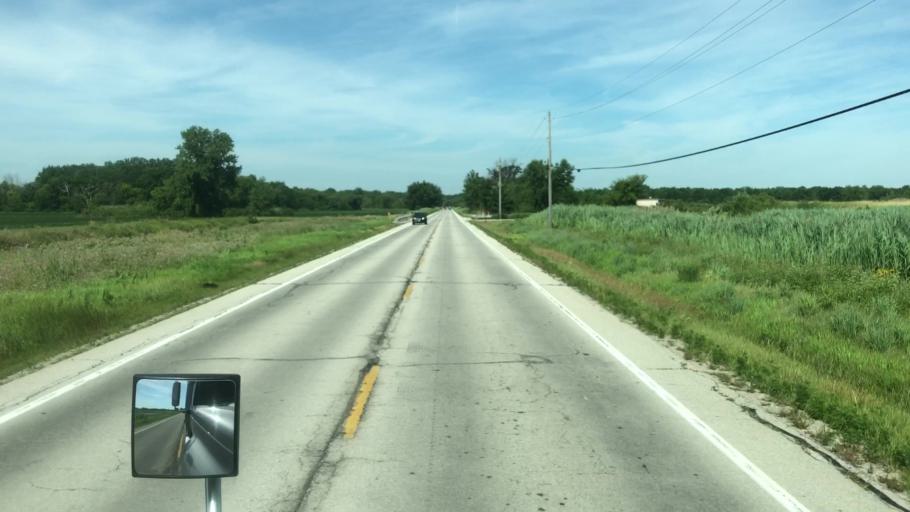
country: US
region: Ohio
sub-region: Ottawa County
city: Port Clinton
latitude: 41.4088
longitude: -82.9429
